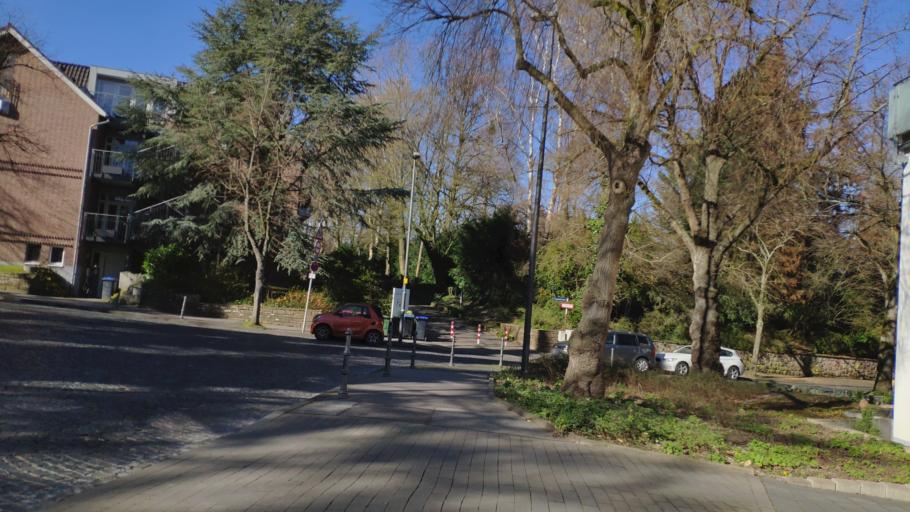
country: DE
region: North Rhine-Westphalia
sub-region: Regierungsbezirk Koln
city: Aachen
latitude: 50.8025
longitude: 6.0545
